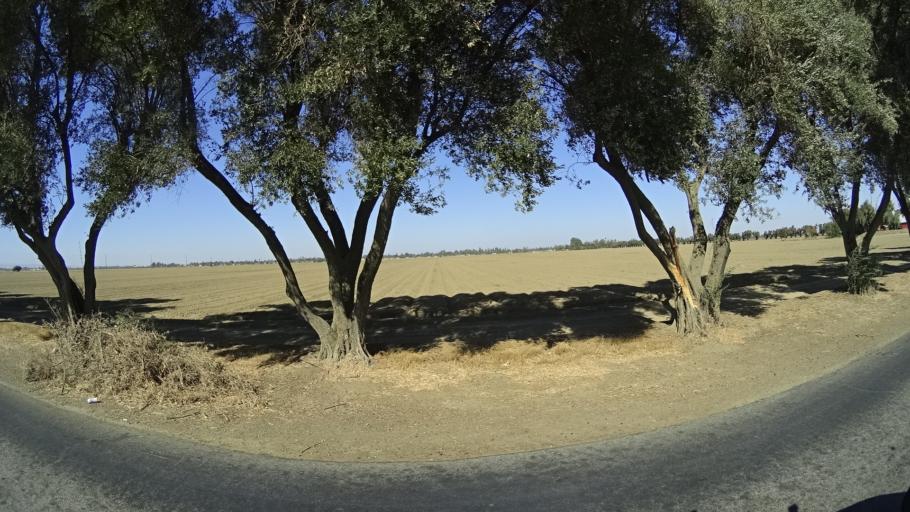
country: US
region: California
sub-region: Yolo County
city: Woodland
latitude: 38.6411
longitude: -121.7885
